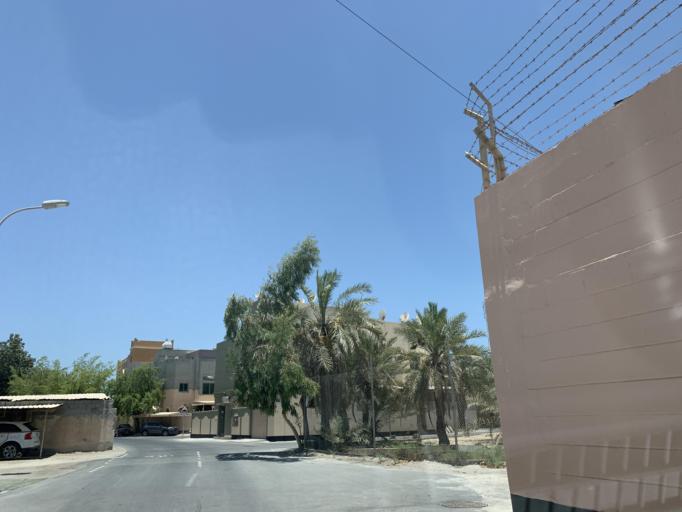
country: BH
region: Manama
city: Jidd Hafs
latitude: 26.2293
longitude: 50.4855
